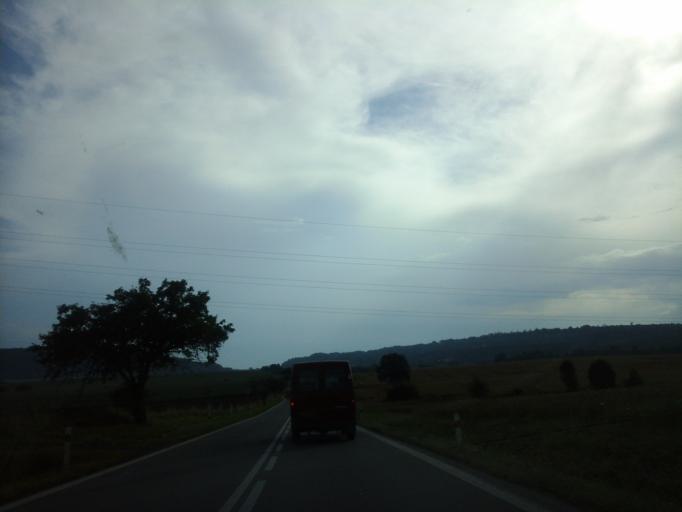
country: CZ
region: Pardubicky
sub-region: Okres Usti nad Orlici
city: Lanskroun
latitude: 49.8901
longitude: 16.5716
